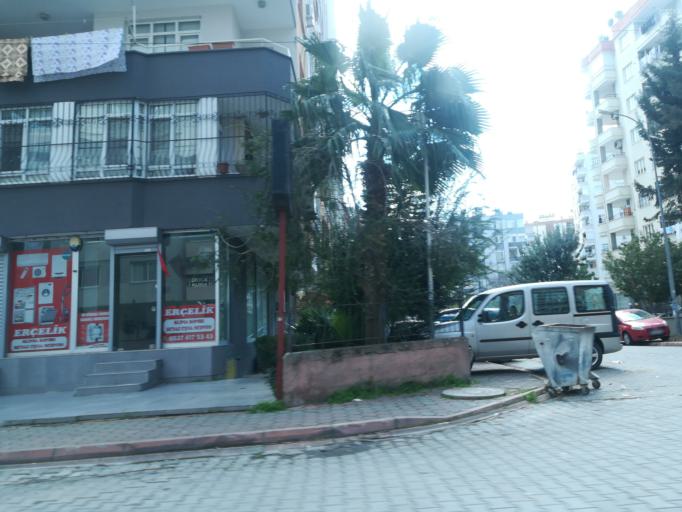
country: TR
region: Adana
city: Adana
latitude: 37.0315
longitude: 35.2981
